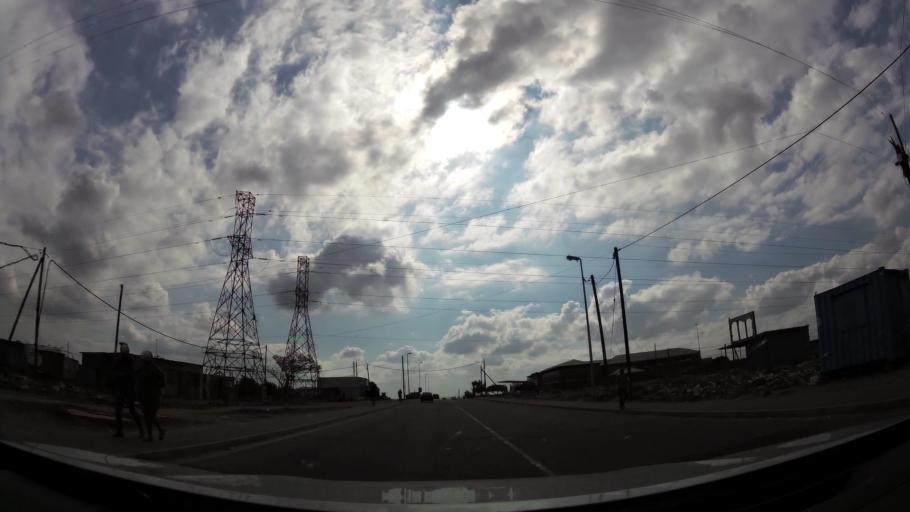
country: ZA
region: Eastern Cape
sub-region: Nelson Mandela Bay Metropolitan Municipality
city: Port Elizabeth
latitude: -33.7980
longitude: 25.5841
